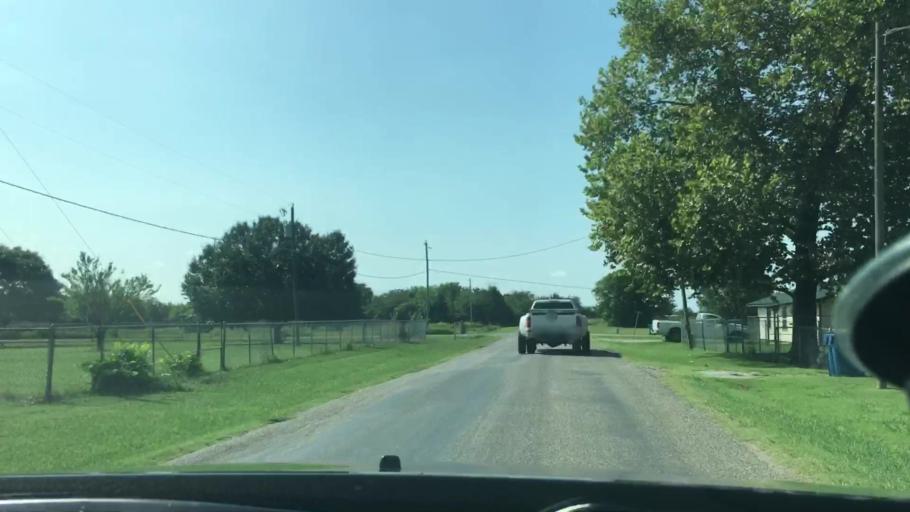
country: US
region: Oklahoma
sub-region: Bryan County
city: Colbert
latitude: 33.9076
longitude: -96.5378
